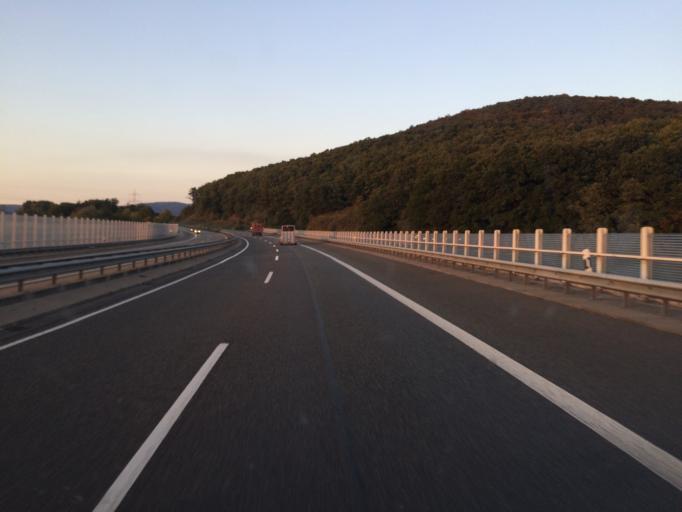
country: DE
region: Rheinland-Pfalz
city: Wartenberg-Rohrbach
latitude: 49.5396
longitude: 7.8544
